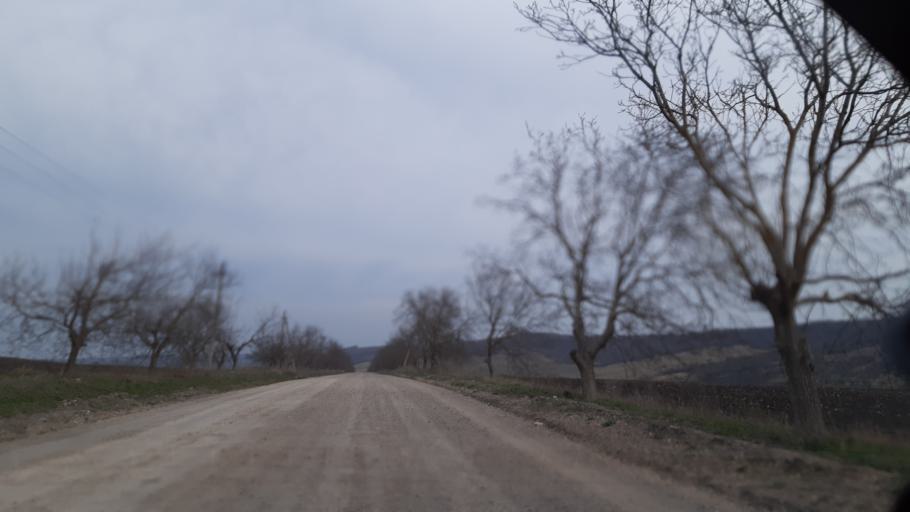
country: MD
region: Soldanesti
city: Soldanesti
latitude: 47.6927
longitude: 28.7370
